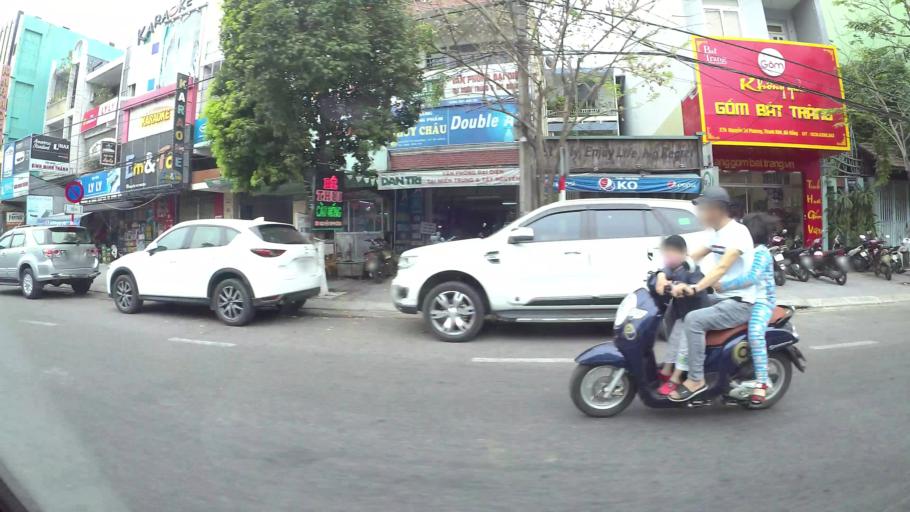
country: VN
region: Da Nang
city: Da Nang
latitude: 16.0579
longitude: 108.2066
